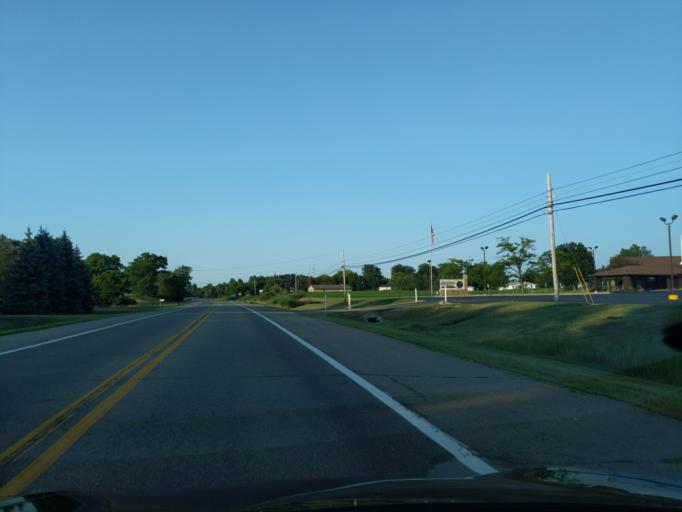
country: US
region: Michigan
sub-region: Shiawassee County
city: Owosso
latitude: 42.9696
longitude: -84.1912
